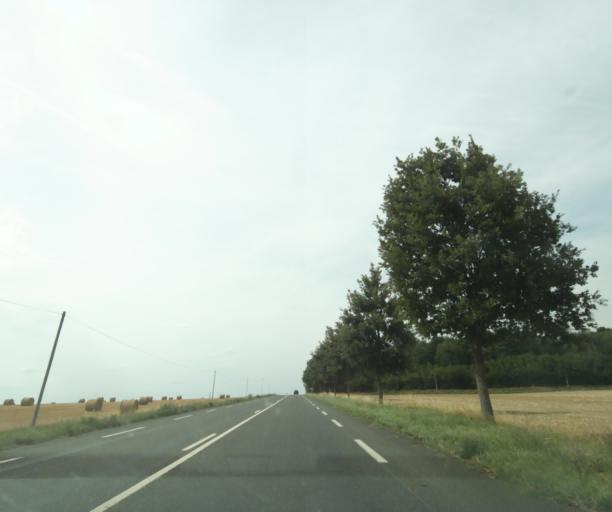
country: FR
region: Centre
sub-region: Departement d'Indre-et-Loire
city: Saint-Christophe-sur-le-Nais
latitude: 47.6514
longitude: 0.4923
